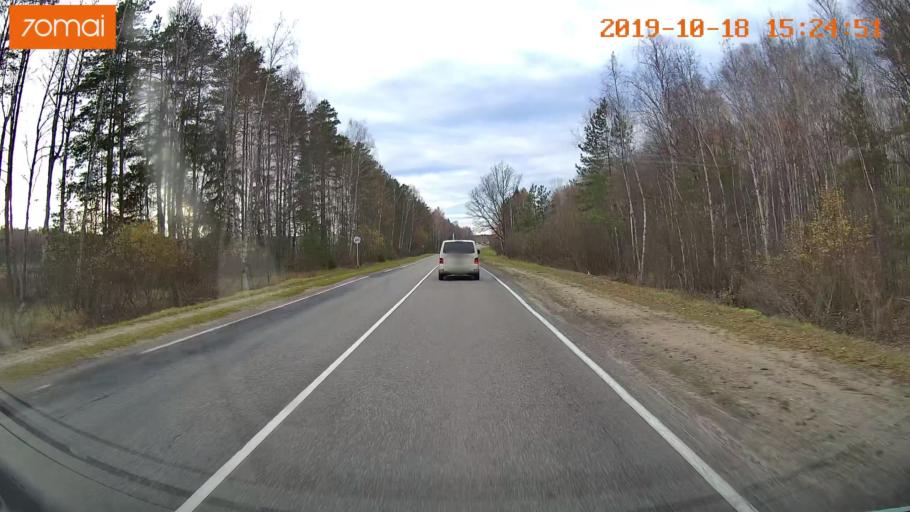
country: RU
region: Vladimir
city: Anopino
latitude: 55.7376
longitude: 40.7163
